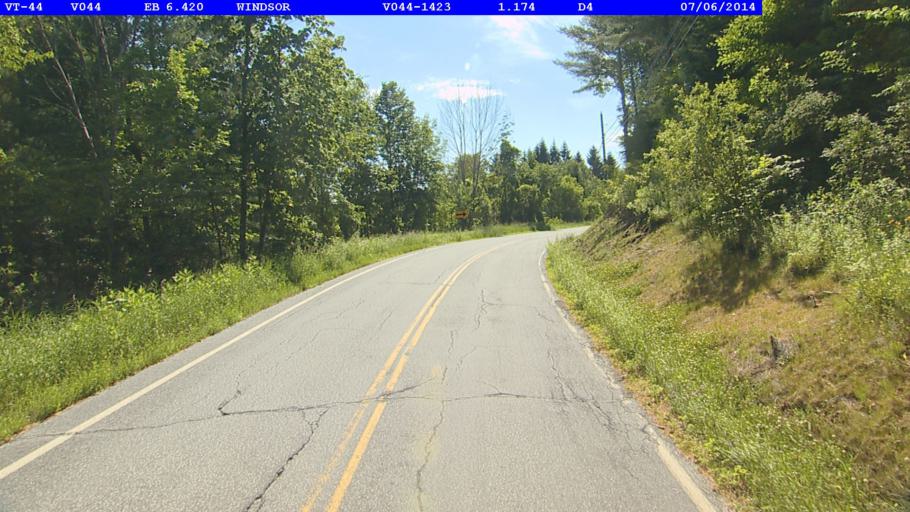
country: US
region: Vermont
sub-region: Windsor County
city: Windsor
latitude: 43.4632
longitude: -72.4308
